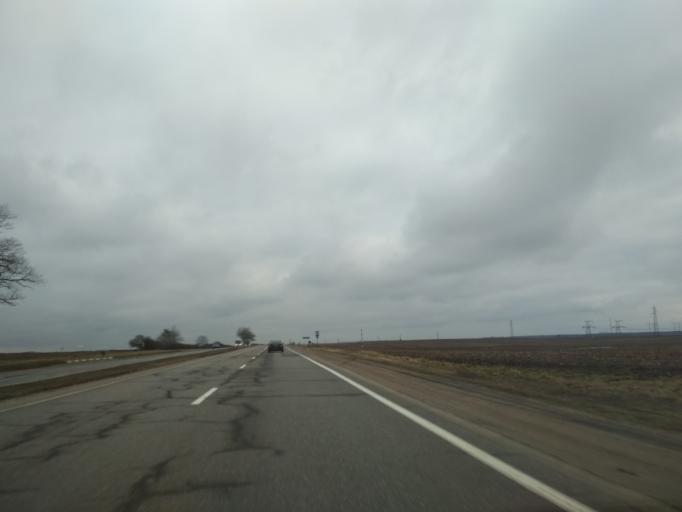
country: BY
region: Minsk
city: Dukora
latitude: 53.6855
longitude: 27.9129
